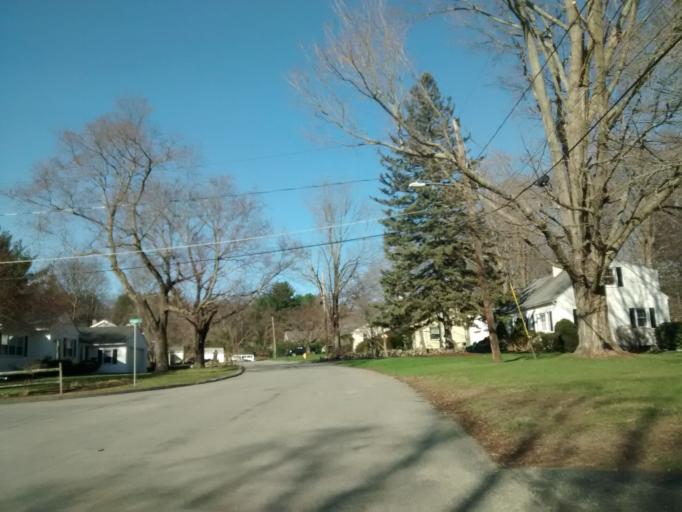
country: US
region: Massachusetts
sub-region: Worcester County
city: Westborough
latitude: 42.2637
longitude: -71.6211
